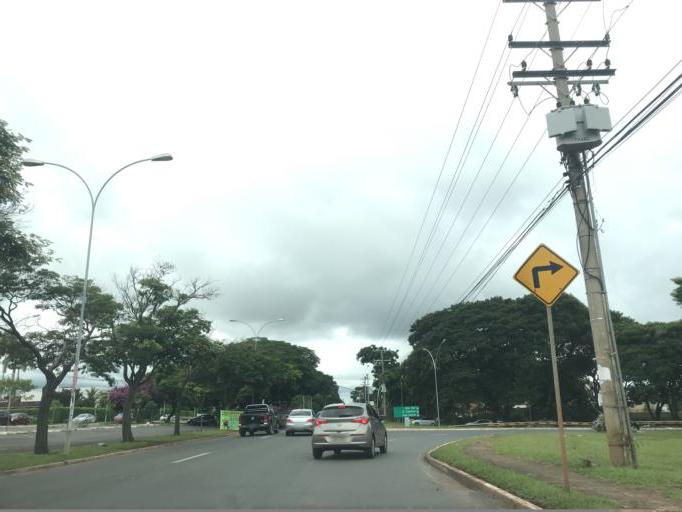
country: BR
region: Federal District
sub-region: Brasilia
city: Brasilia
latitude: -15.8452
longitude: -47.8955
